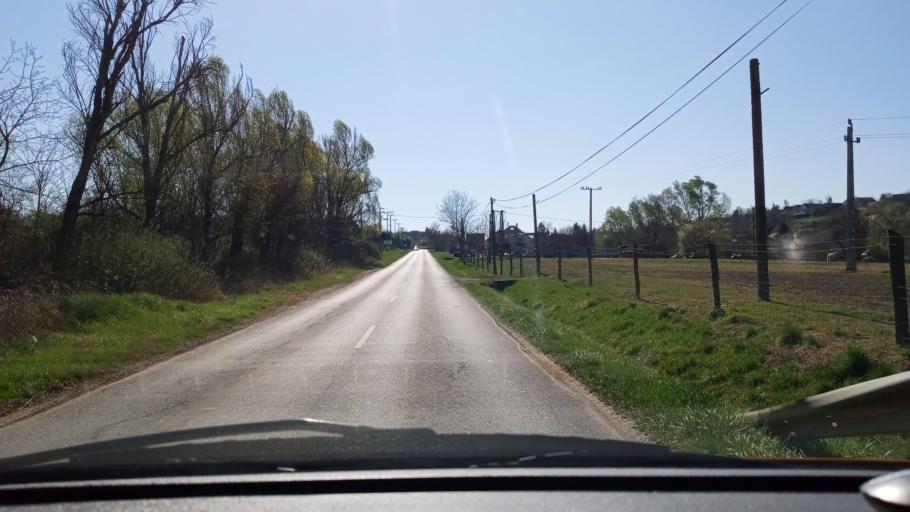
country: HU
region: Baranya
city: Pecs
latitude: 46.0889
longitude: 18.2835
